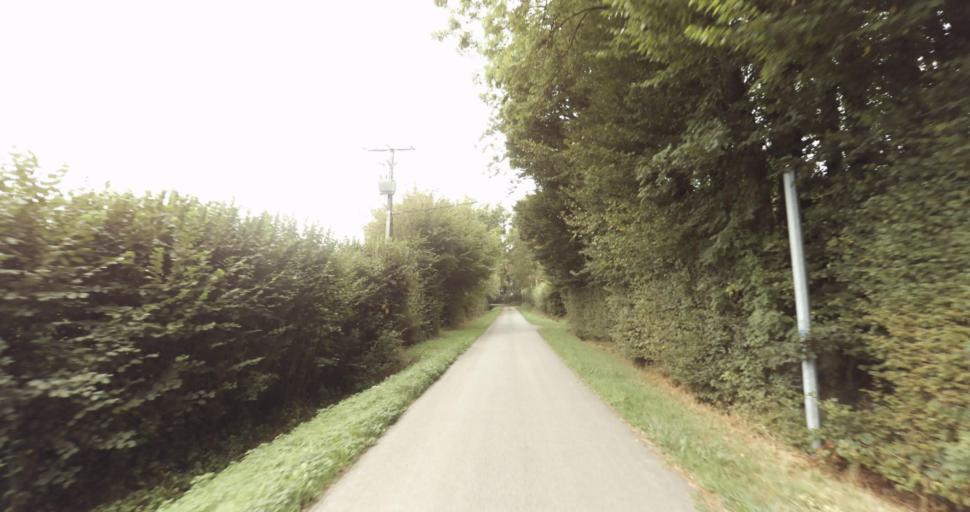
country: FR
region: Lower Normandy
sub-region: Departement de l'Orne
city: Gace
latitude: 48.7515
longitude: 0.3140
